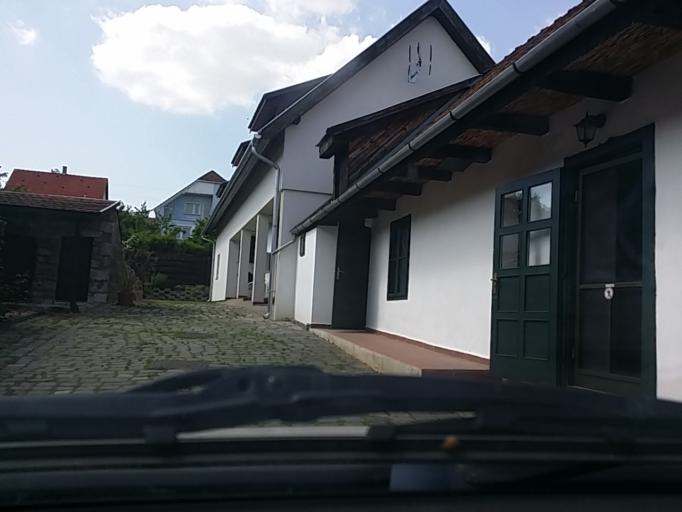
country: HU
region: Pest
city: Pilisszentkereszt
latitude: 47.6925
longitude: 18.9009
